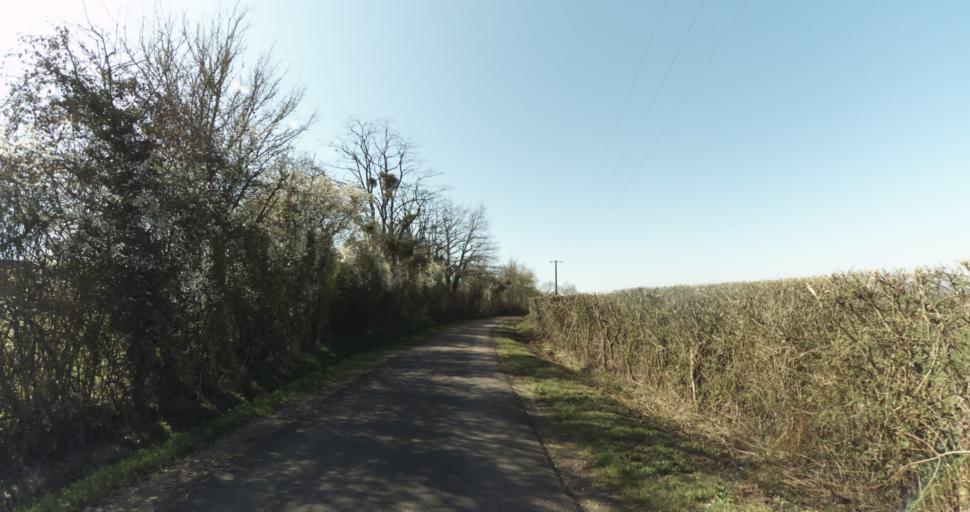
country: FR
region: Lower Normandy
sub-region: Departement du Calvados
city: Livarot
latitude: 48.9791
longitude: 0.0602
